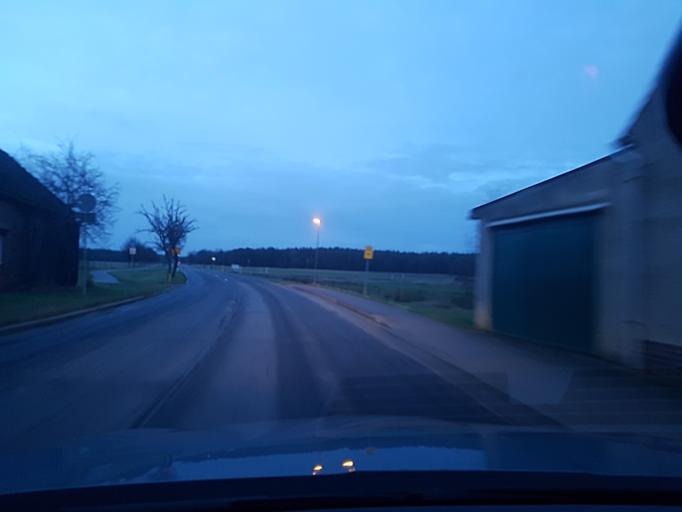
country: DE
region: Brandenburg
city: Ruckersdorf
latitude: 51.5754
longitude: 13.5641
